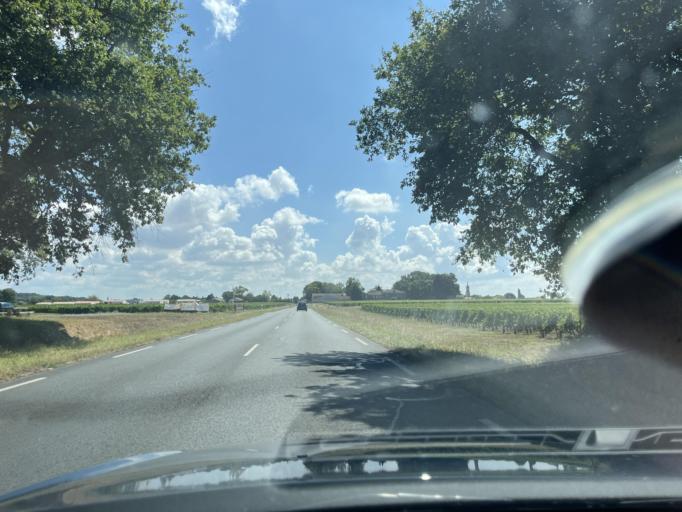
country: FR
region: Aquitaine
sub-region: Departement de la Gironde
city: Bourg
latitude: 45.0587
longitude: -0.6050
